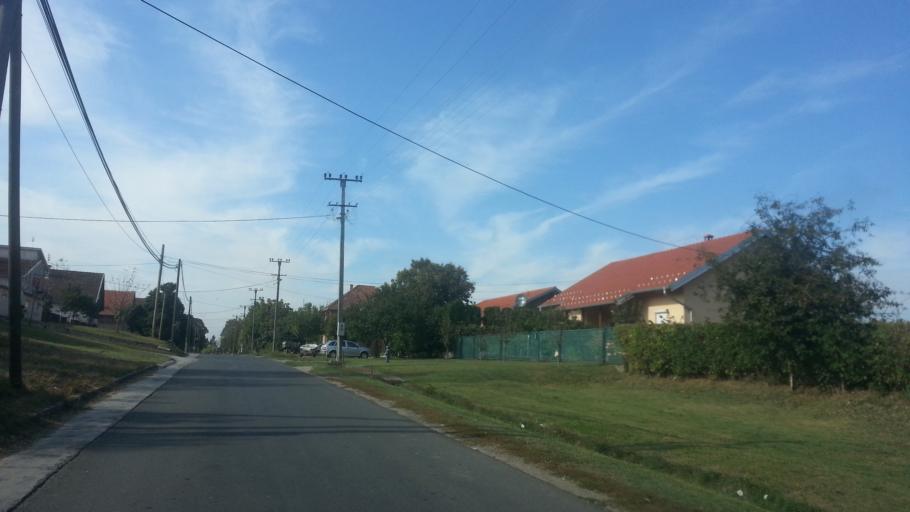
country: RS
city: Belegis
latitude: 45.0143
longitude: 20.3241
